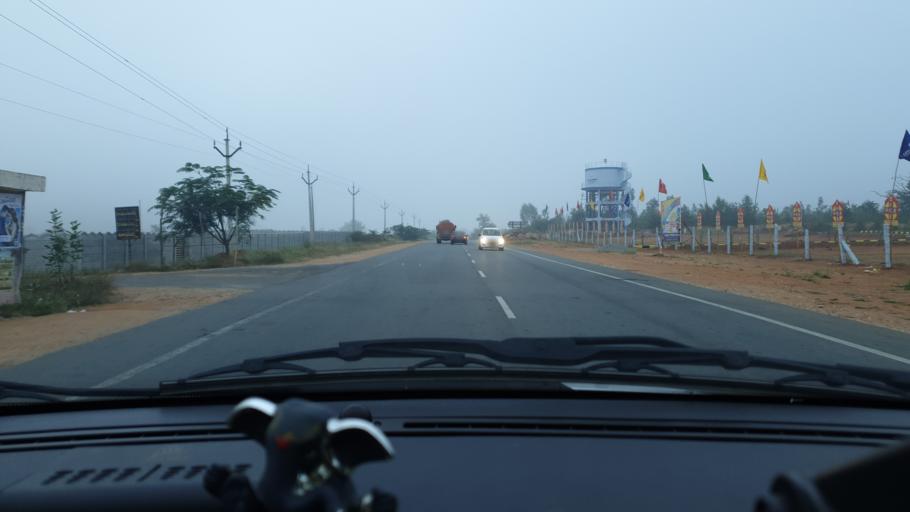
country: IN
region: Telangana
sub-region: Mahbubnagar
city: Farrukhnagar
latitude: 16.9171
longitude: 78.5271
